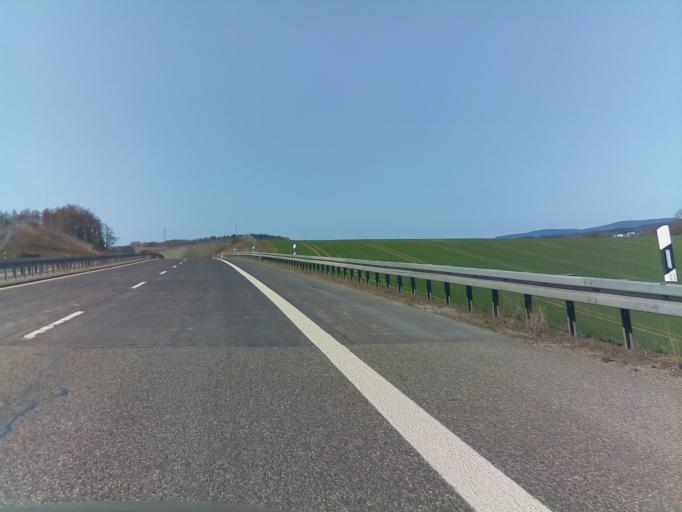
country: DE
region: Thuringia
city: Eisfeld
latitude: 50.4487
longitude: 10.8707
